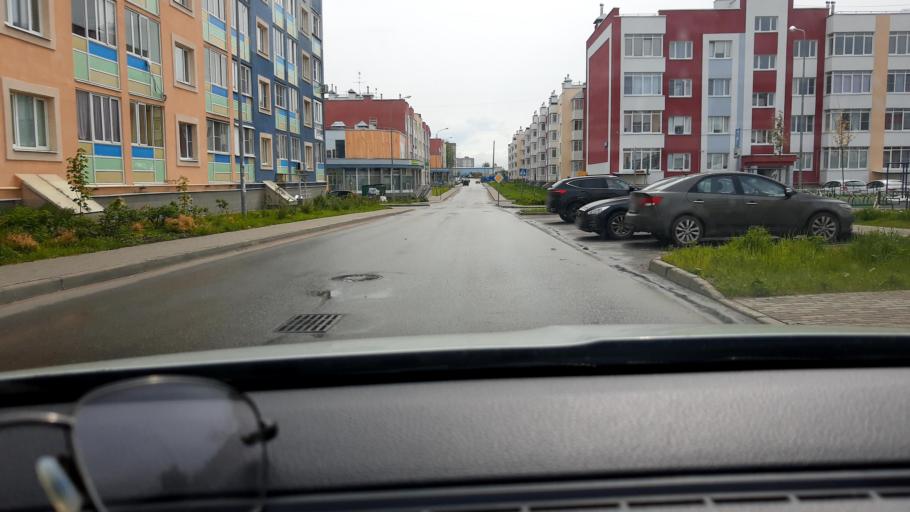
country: RU
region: Moskovskaya
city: Dedovsk
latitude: 55.8399
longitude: 37.1297
